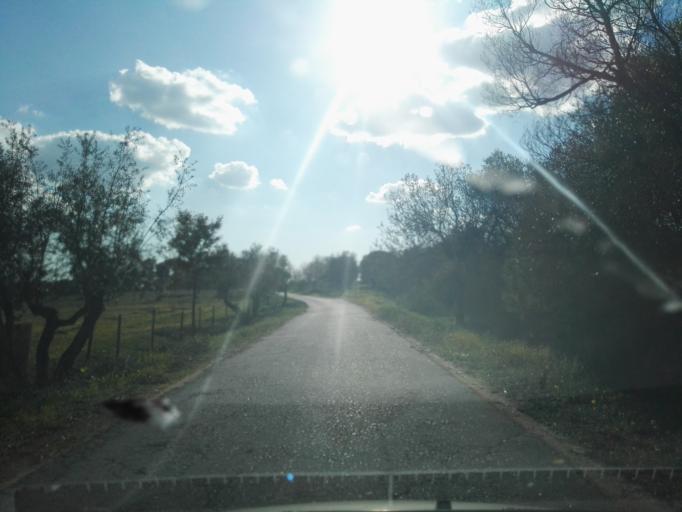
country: PT
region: Evora
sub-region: Evora
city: Evora
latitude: 38.5370
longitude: -7.9416
